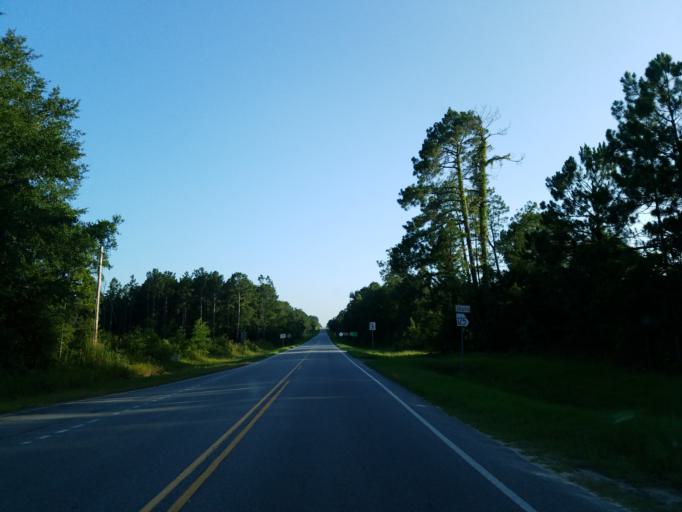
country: US
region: Georgia
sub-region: Ben Hill County
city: Fitzgerald
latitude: 31.6985
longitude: -83.3027
